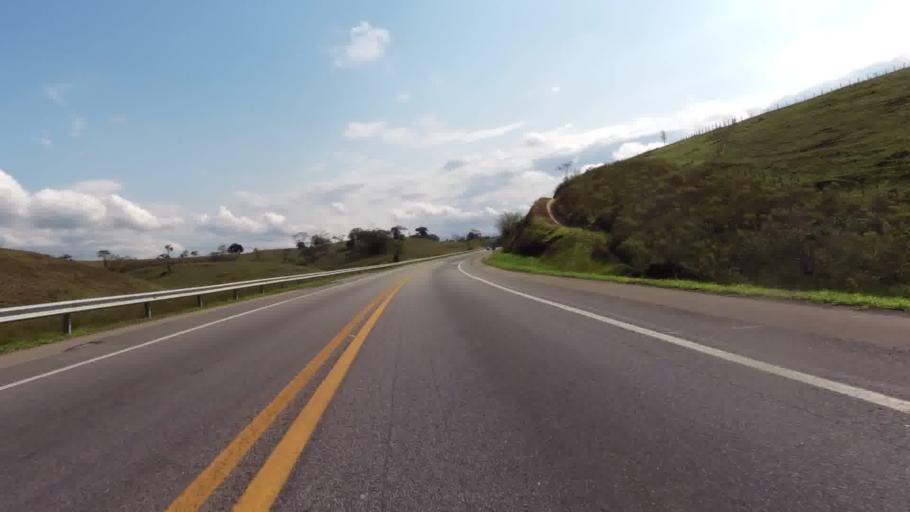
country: BR
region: Rio de Janeiro
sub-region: Macae
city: Macae
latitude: -22.2526
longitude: -41.8233
